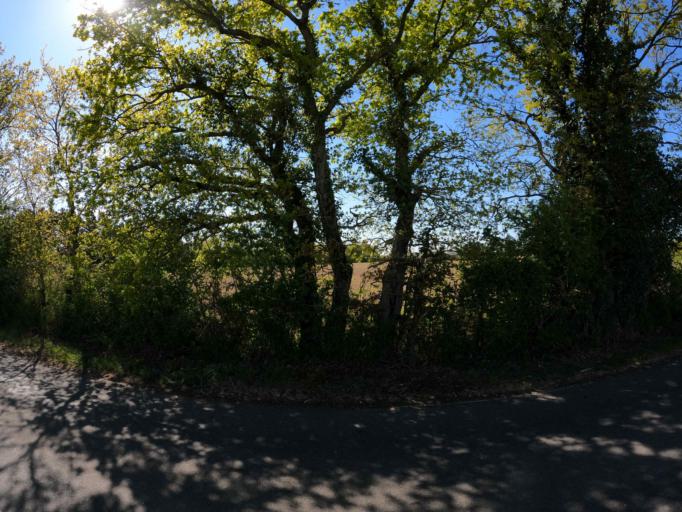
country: FR
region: Pays de la Loire
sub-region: Departement de la Loire-Atlantique
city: Gorges
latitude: 47.1124
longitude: -1.2947
